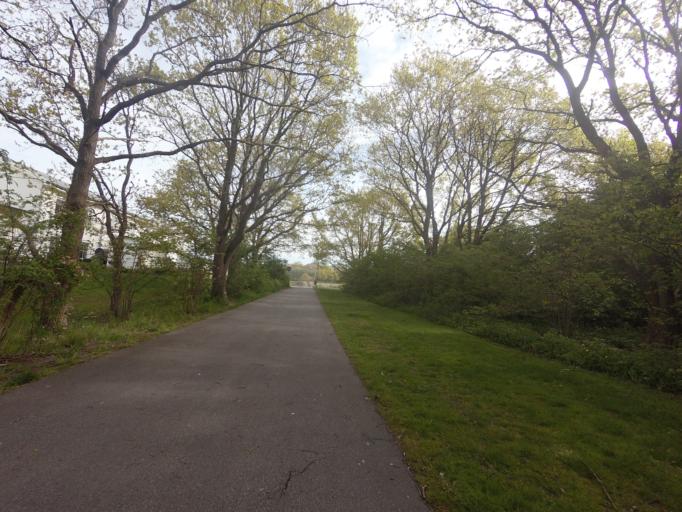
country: SE
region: Skane
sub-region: Hoganas Kommun
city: Hoganas
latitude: 56.1946
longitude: 12.5810
